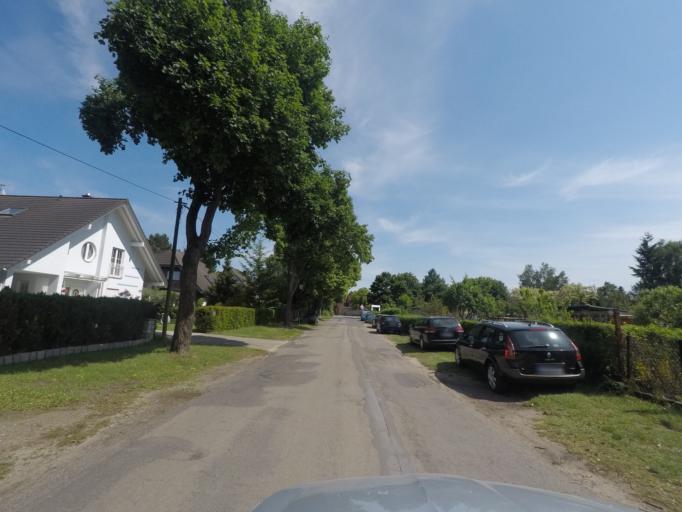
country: DE
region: Brandenburg
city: Melchow
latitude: 52.8471
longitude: 13.7188
